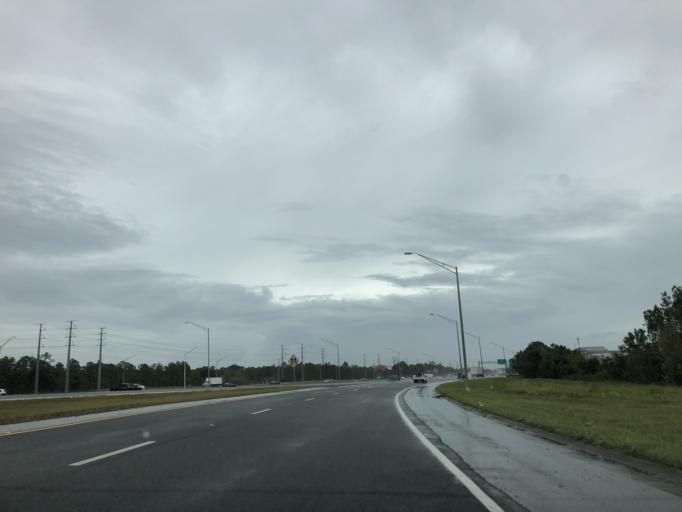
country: US
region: Florida
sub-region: Osceola County
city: Celebration
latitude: 28.3082
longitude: -81.5673
